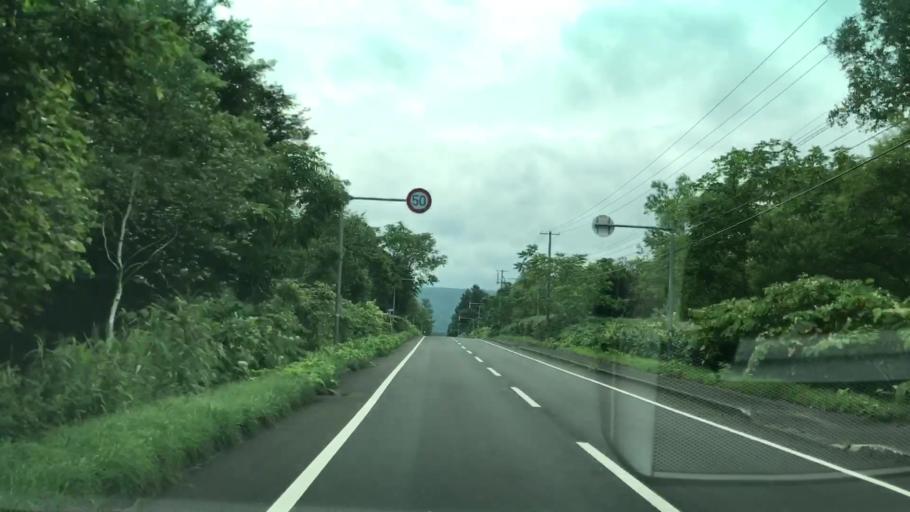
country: JP
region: Hokkaido
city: Yoichi
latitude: 43.0690
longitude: 140.8186
